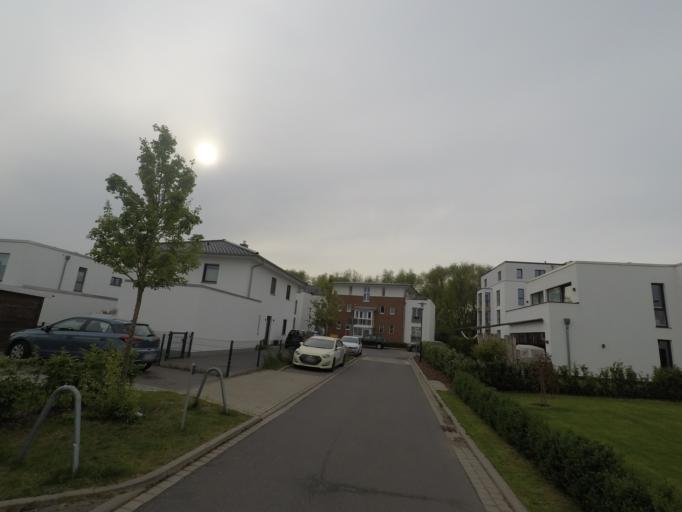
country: DE
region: Mecklenburg-Vorpommern
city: Rostock
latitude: 54.0647
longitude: 12.1296
